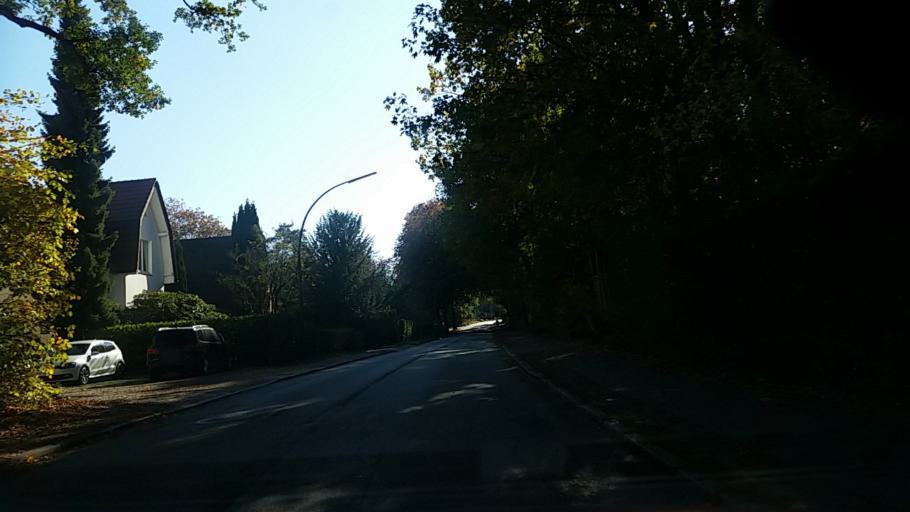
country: DE
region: Schleswig-Holstein
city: Halstenbek
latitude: 53.5728
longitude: 9.8072
